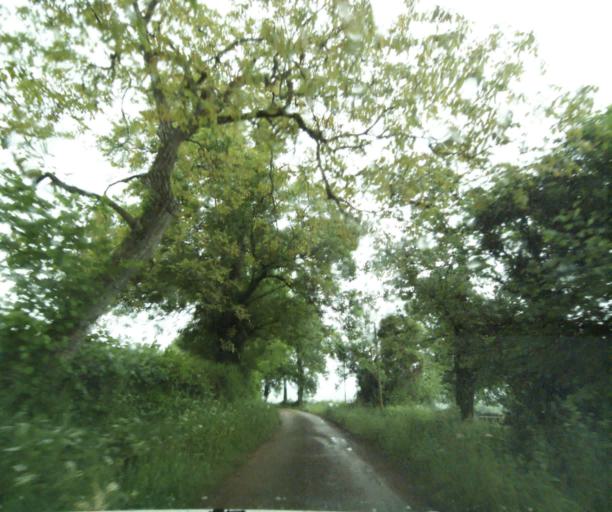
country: FR
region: Bourgogne
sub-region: Departement de Saone-et-Loire
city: La Clayette
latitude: 46.3591
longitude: 4.3649
